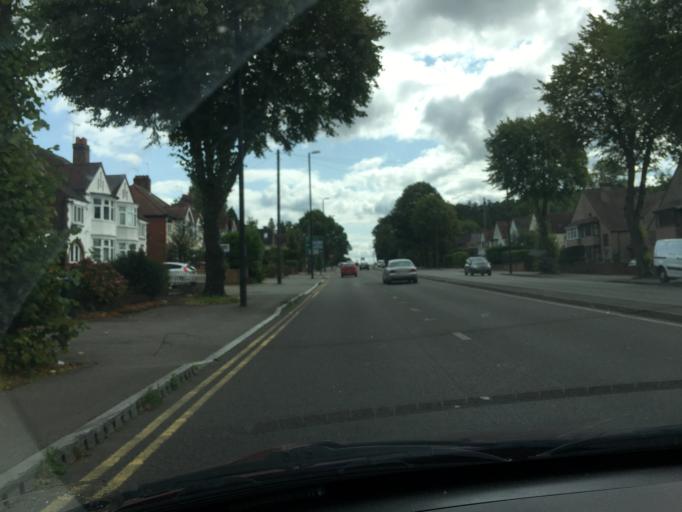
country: GB
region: England
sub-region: Coventry
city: Coventry
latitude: 52.3878
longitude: -1.5388
